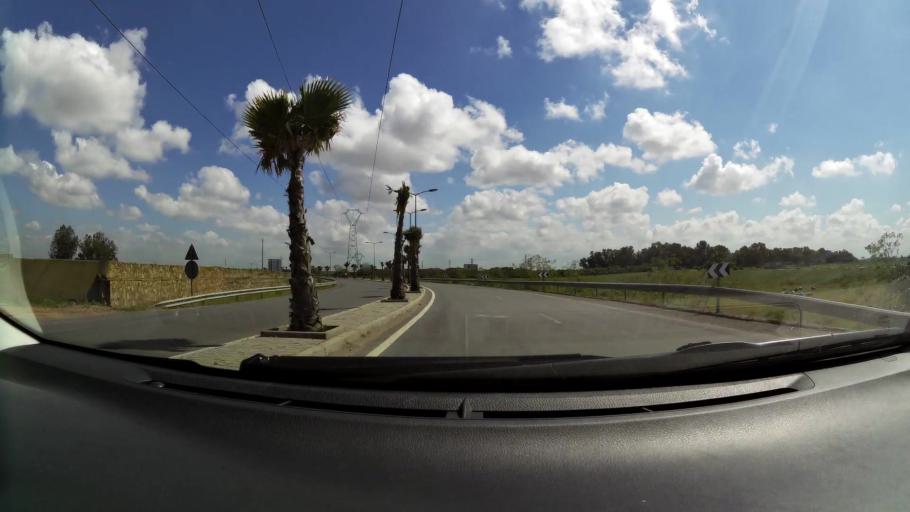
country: MA
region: Grand Casablanca
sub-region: Nouaceur
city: Bouskoura
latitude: 33.5061
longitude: -7.6112
